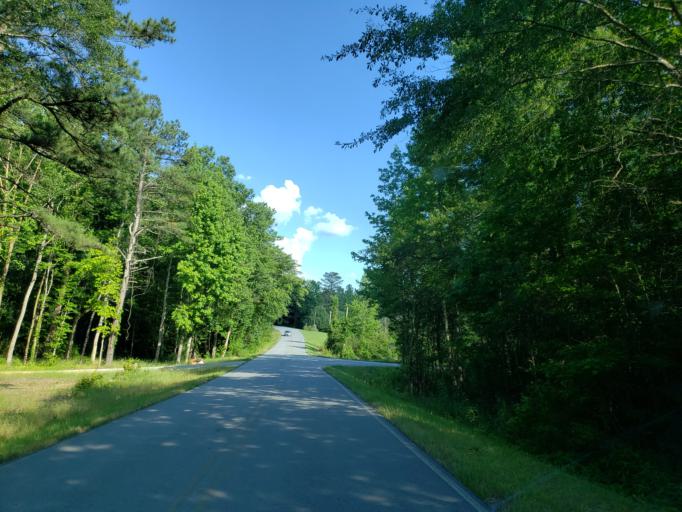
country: US
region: Georgia
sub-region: Haralson County
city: Bremen
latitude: 33.6864
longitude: -85.0969
